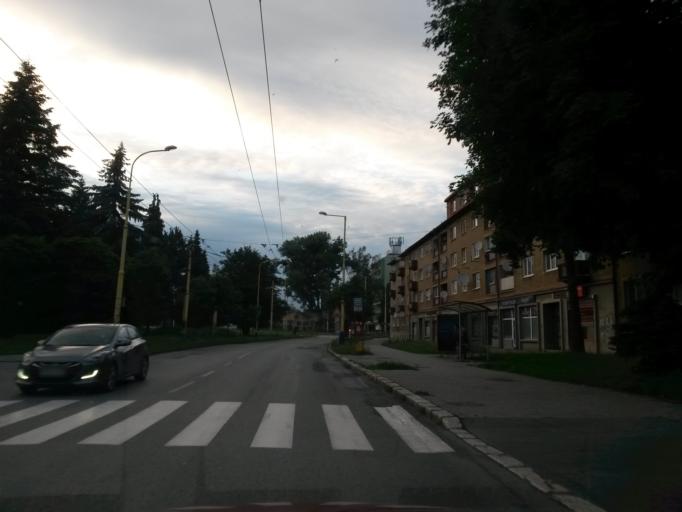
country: SK
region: Presovsky
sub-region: Okres Presov
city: Presov
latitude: 48.9936
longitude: 21.2326
